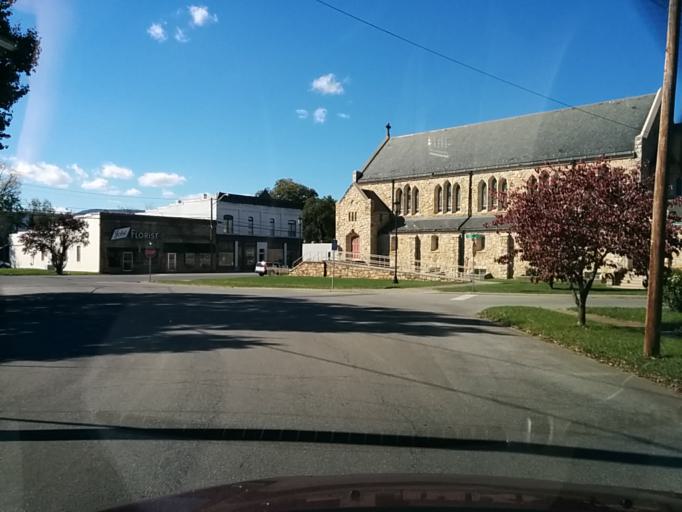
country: US
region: Virginia
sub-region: City of Salem
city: Salem
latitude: 37.2913
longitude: -80.0534
